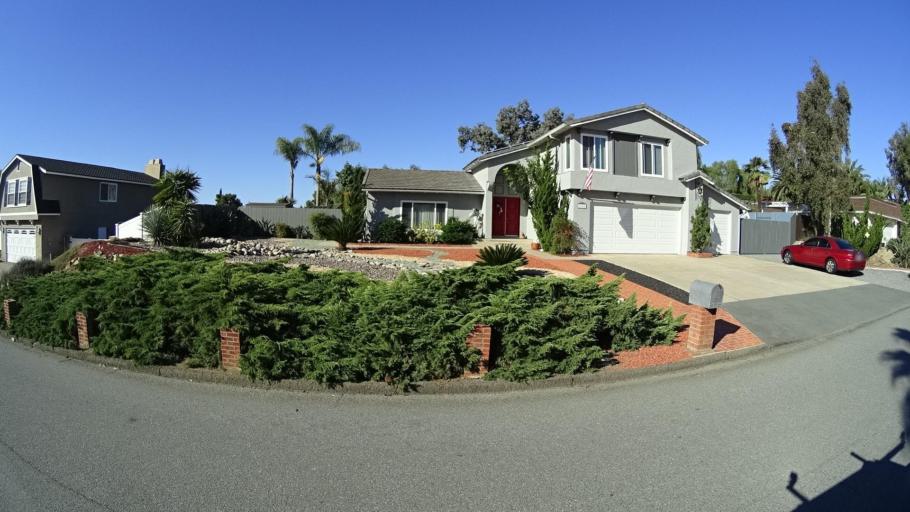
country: US
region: California
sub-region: San Diego County
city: Bonita
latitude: 32.6823
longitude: -117.0197
